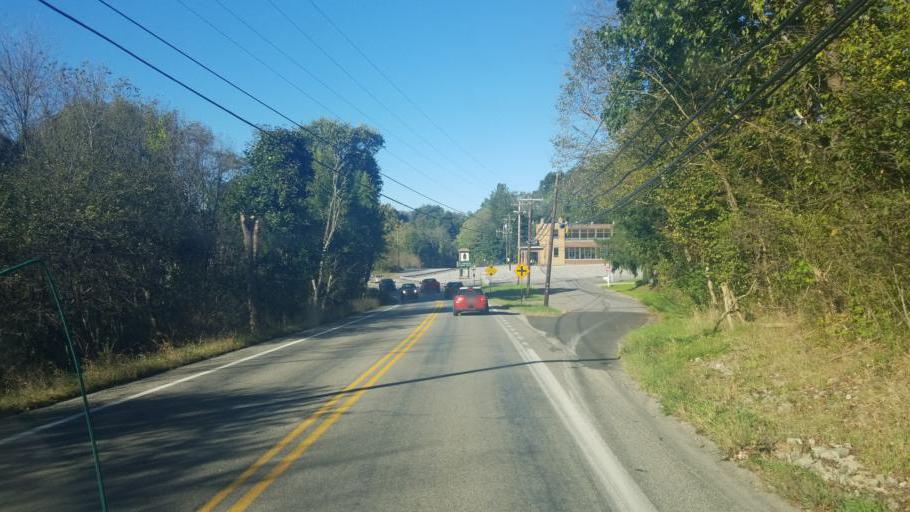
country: US
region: Pennsylvania
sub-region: Allegheny County
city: Imperial
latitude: 40.4466
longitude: -80.2446
